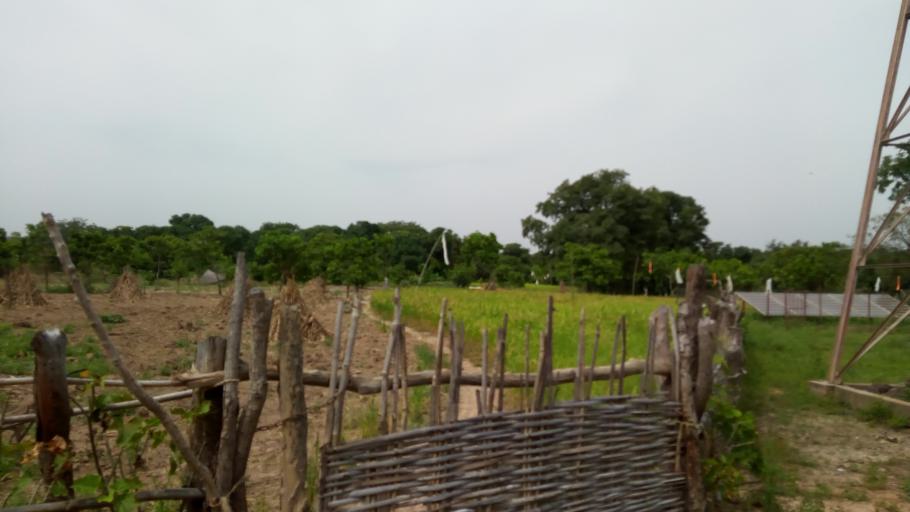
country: ML
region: Koulikoro
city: Kangaba
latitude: 11.4991
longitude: -8.5497
